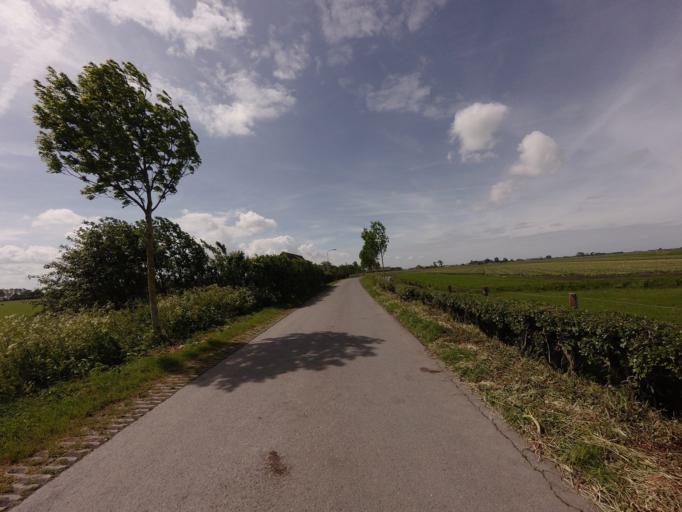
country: NL
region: North Holland
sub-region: Gemeente Opmeer
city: Opmeer
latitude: 52.6712
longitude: 4.9791
